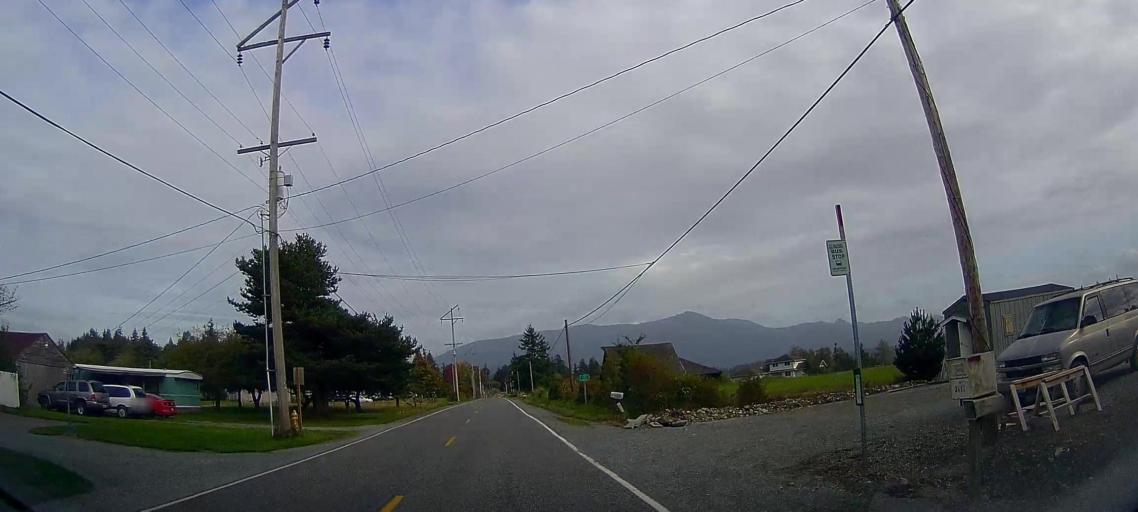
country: US
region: Washington
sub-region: Skagit County
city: Burlington
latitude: 48.4537
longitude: -122.2975
